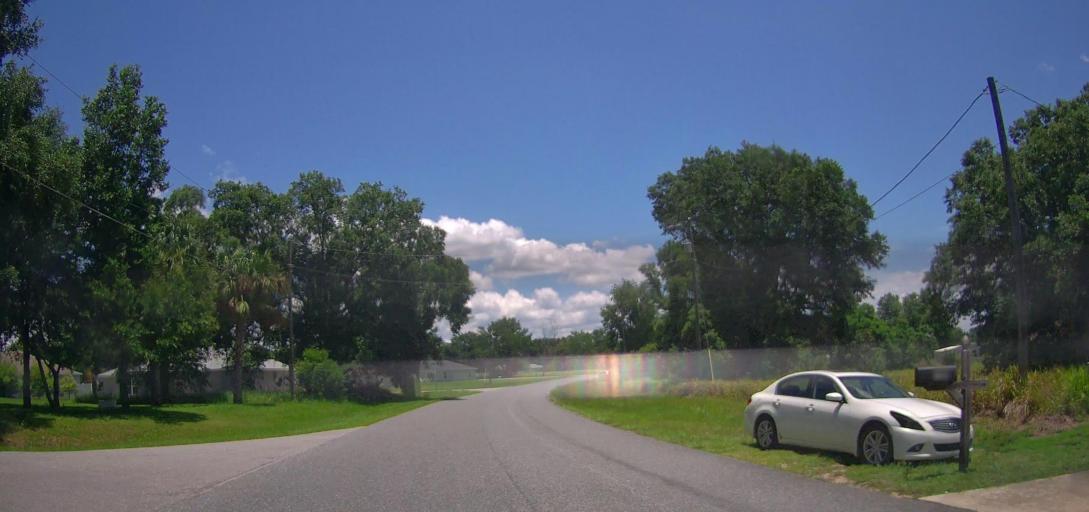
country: US
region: Florida
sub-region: Marion County
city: Silver Springs Shores
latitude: 29.1277
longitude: -82.0493
